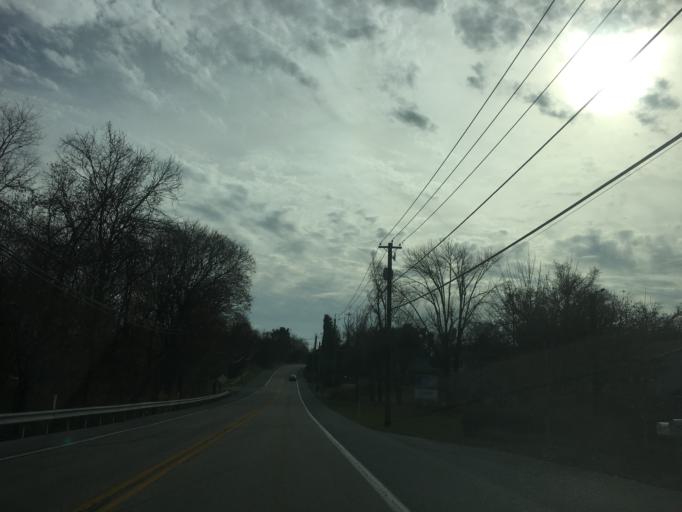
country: US
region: Pennsylvania
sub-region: Dauphin County
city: Colonial Park
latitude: 40.3176
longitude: -76.8232
